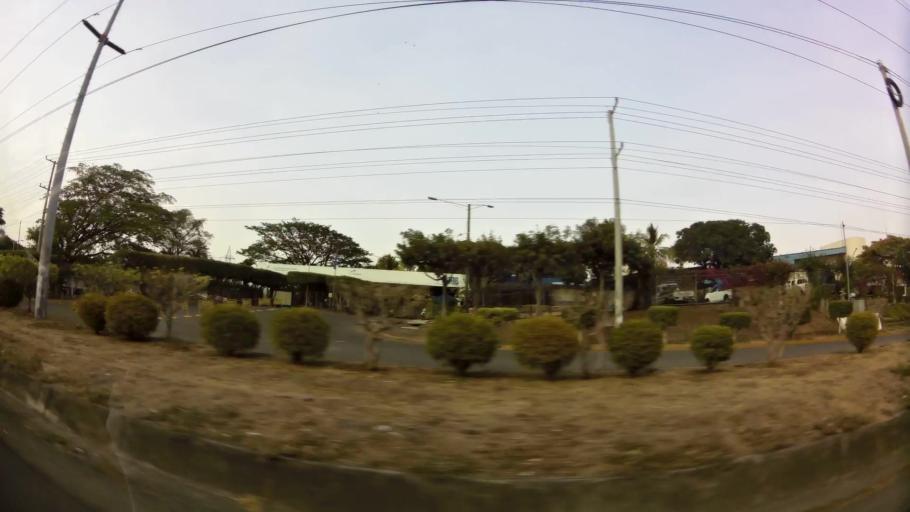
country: NI
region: Managua
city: Ciudad Sandino
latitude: 12.1650
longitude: -86.3408
